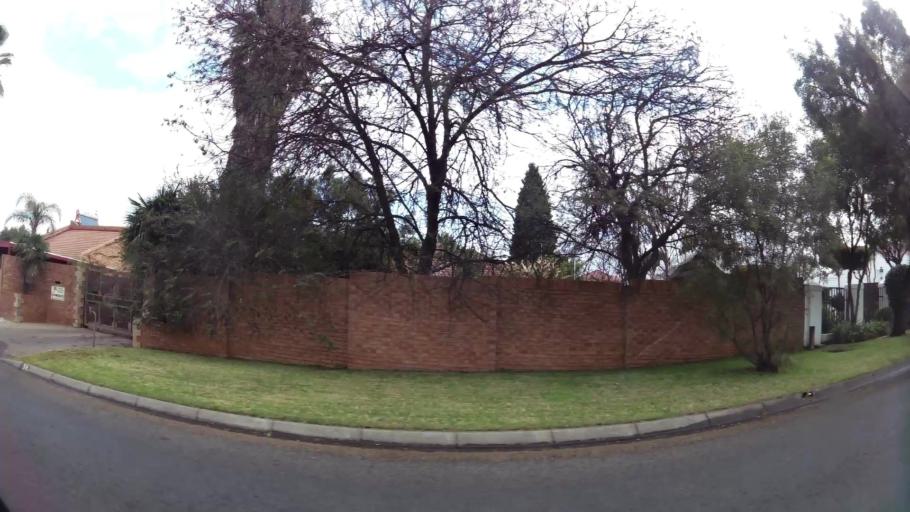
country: ZA
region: Gauteng
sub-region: Sedibeng District Municipality
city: Vanderbijlpark
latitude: -26.7423
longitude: 27.8546
